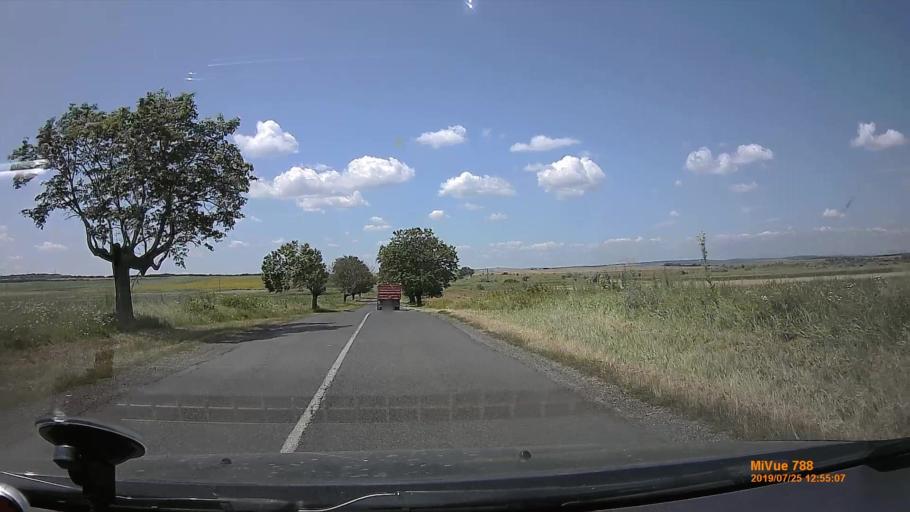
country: HU
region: Borsod-Abauj-Zemplen
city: Abaujszanto
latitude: 48.3095
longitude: 21.1909
